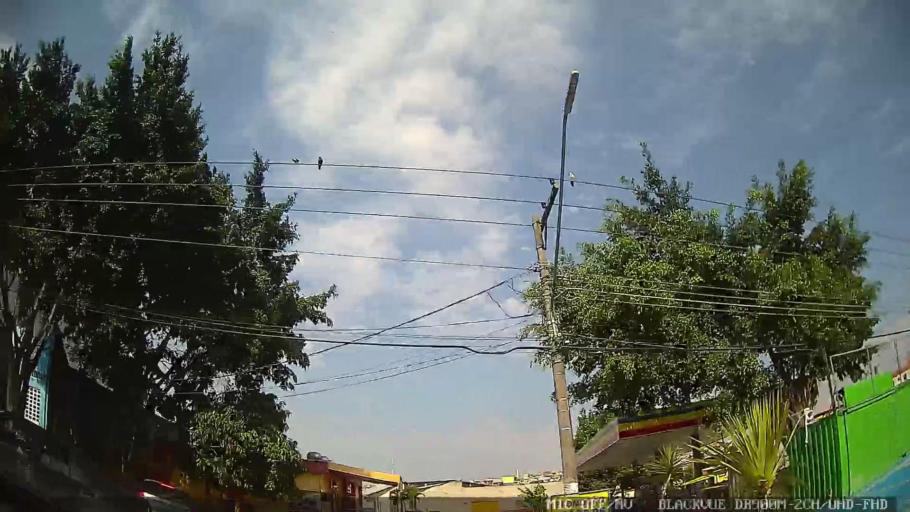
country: BR
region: Sao Paulo
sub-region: Ferraz De Vasconcelos
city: Ferraz de Vasconcelos
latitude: -23.5279
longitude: -46.4178
